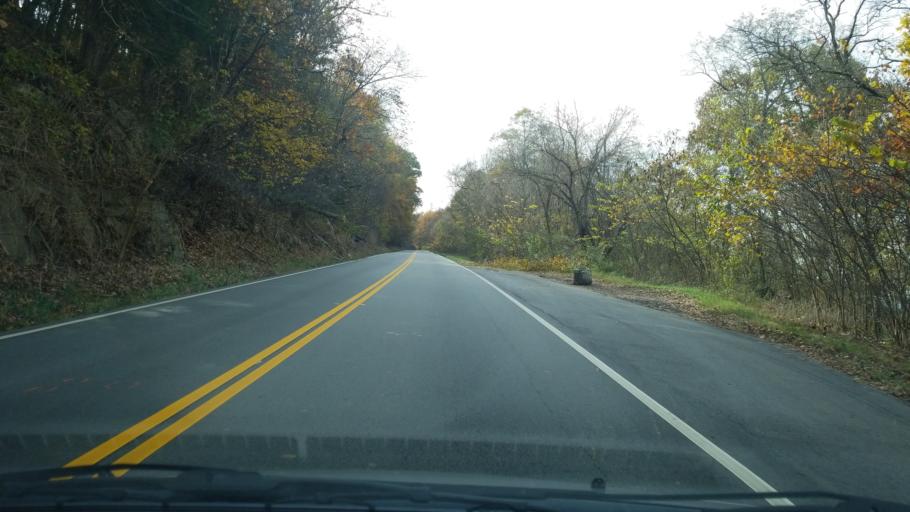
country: US
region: Georgia
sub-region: Dade County
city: Trenton
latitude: 34.8459
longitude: -85.4966
